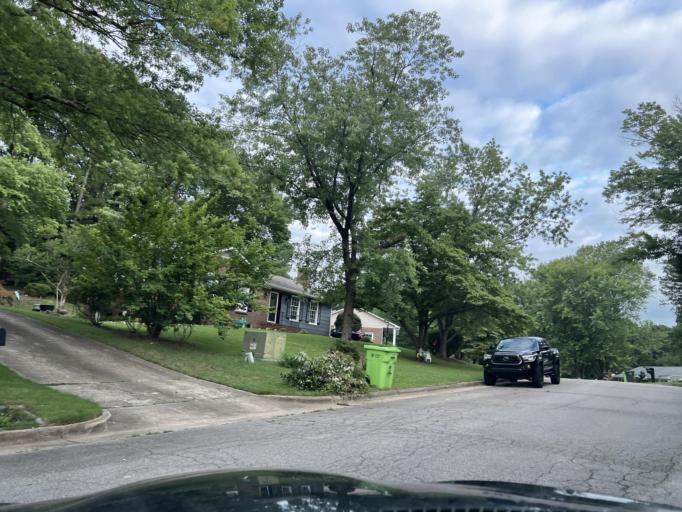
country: US
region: North Carolina
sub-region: Wake County
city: West Raleigh
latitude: 35.8612
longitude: -78.6550
